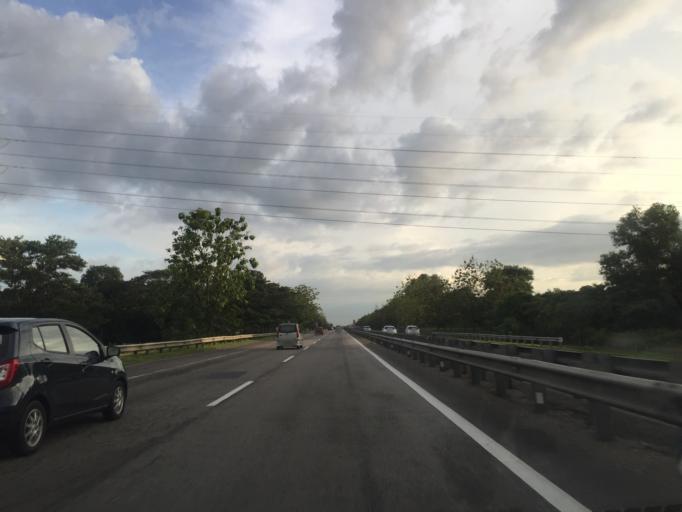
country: MY
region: Kedah
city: Bedong
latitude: 5.7766
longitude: 100.5033
